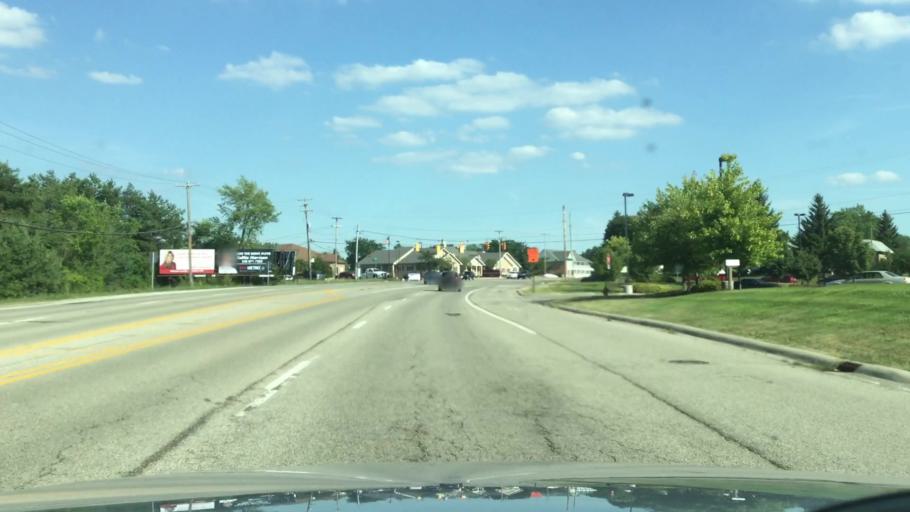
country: US
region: Michigan
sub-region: Genesee County
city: Grand Blanc
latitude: 42.9100
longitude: -83.6056
